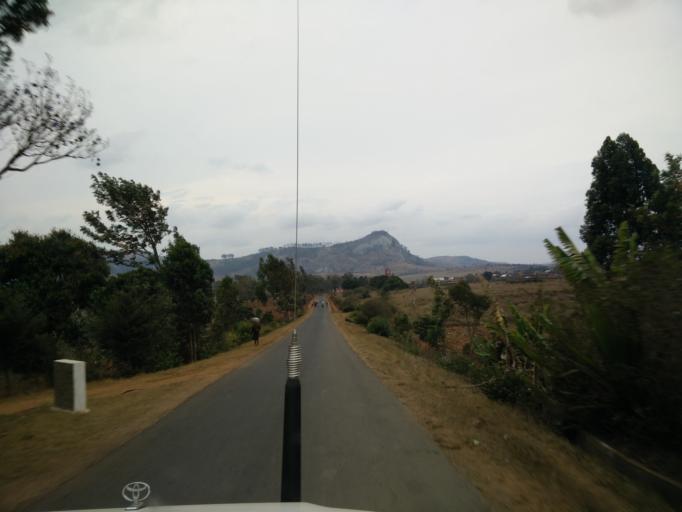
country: MG
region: Upper Matsiatra
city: Fianarantsoa
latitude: -21.5967
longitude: 47.0069
